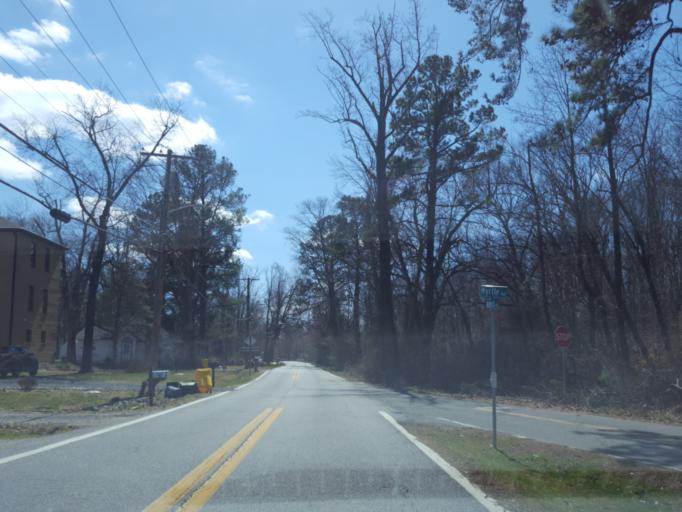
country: US
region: Maryland
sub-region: Calvert County
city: North Beach
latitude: 38.7214
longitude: -76.5280
